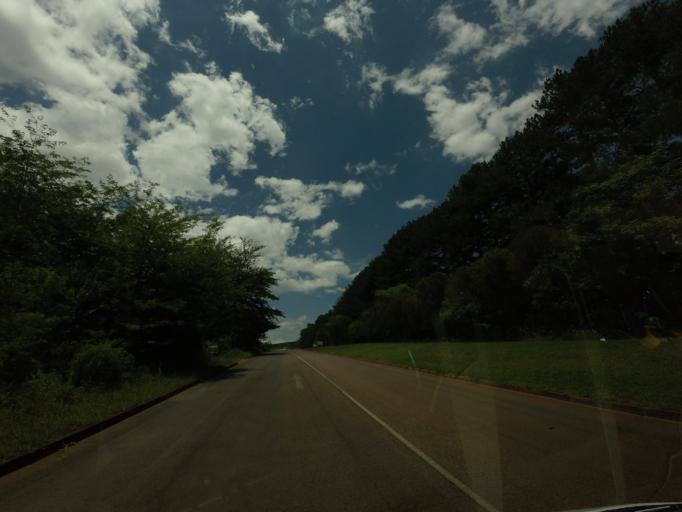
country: ZA
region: Mpumalanga
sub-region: Ehlanzeni District
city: Graksop
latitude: -25.0853
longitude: 30.7851
